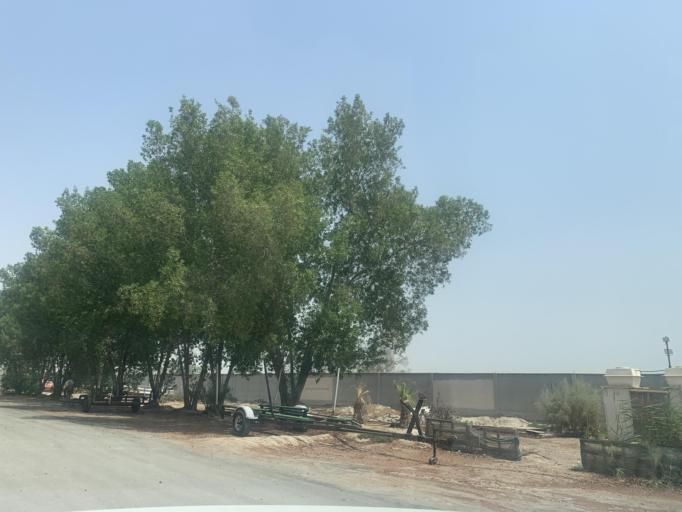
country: BH
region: Central Governorate
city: Madinat Hamad
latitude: 26.1225
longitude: 50.4622
